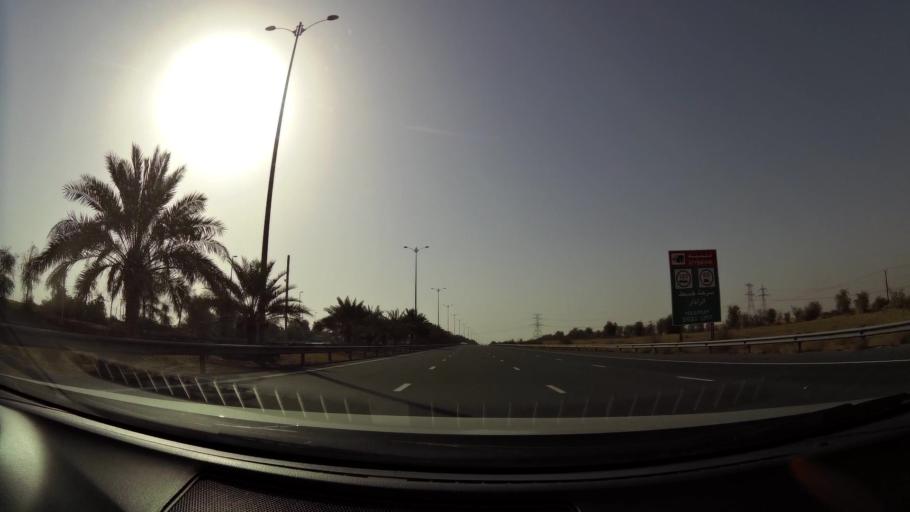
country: OM
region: Al Buraimi
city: Al Buraymi
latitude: 24.6582
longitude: 55.6894
